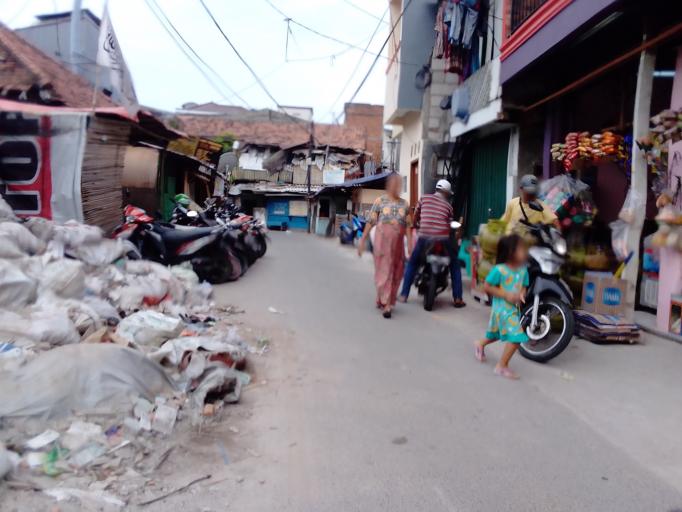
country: ID
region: Jakarta Raya
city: Jakarta
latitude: -6.1562
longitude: 106.8116
